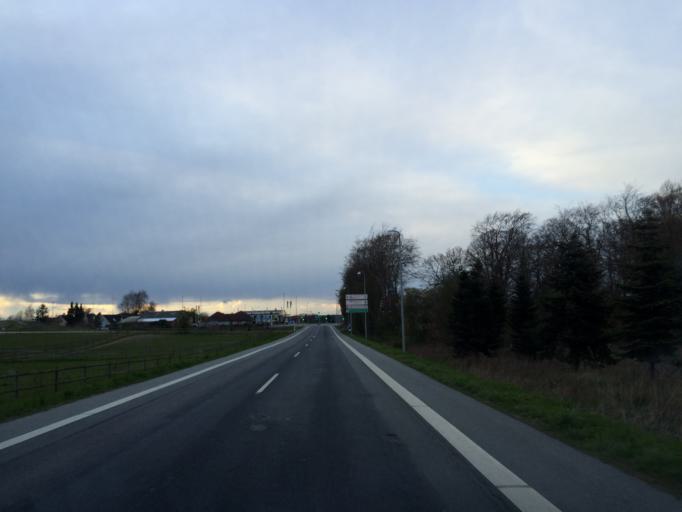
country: DK
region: South Denmark
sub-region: Odense Kommune
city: Bellinge
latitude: 55.3878
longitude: 10.2626
